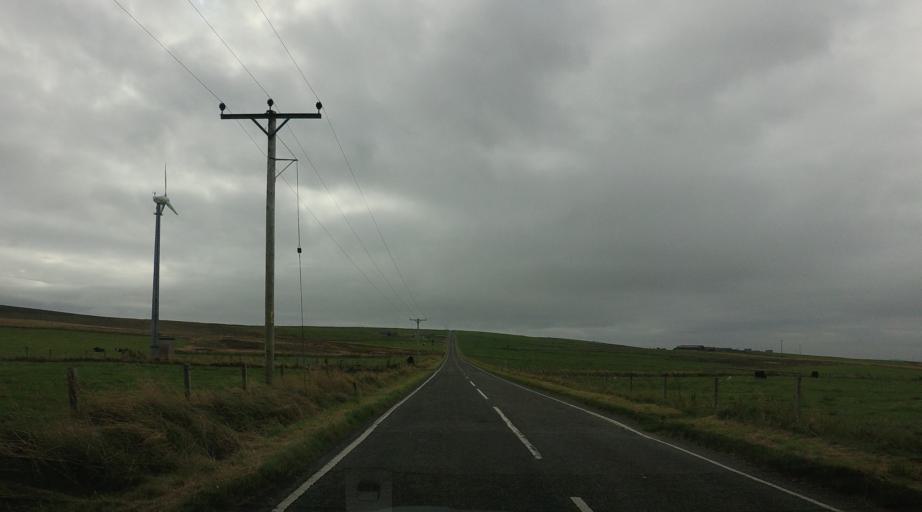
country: GB
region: Scotland
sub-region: Orkney Islands
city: Orkney
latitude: 58.7848
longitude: -2.9586
